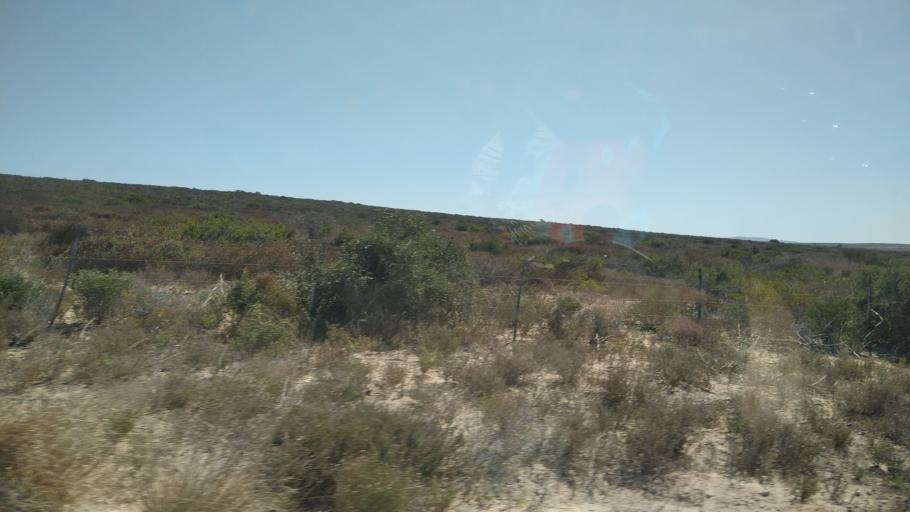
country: ZA
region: Western Cape
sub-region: West Coast District Municipality
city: Vredenburg
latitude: -33.0039
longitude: 18.1237
